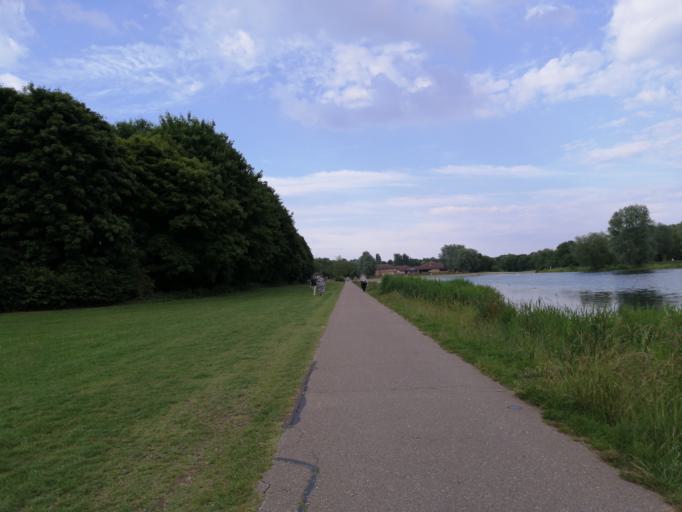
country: GB
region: England
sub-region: Peterborough
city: Peterborough
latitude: 52.5681
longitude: -0.2725
